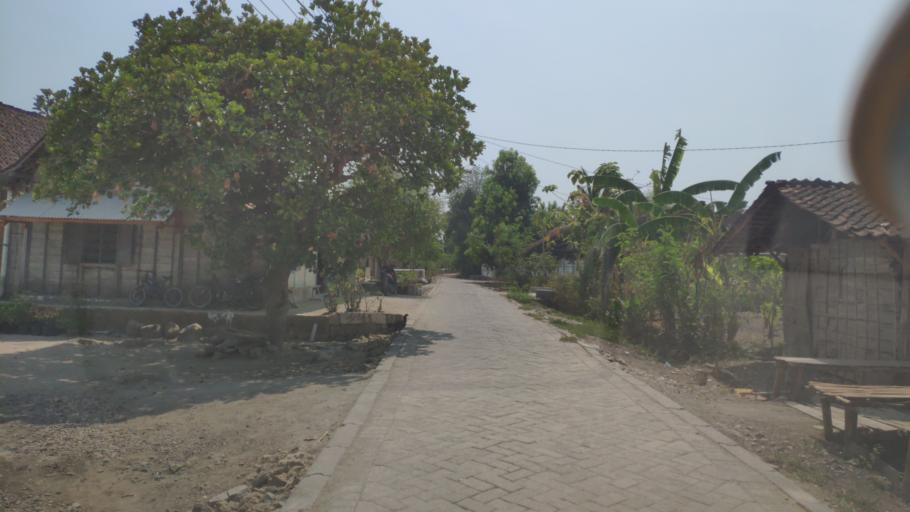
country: ID
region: Central Java
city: Mendenrejo
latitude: -7.2417
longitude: 111.4292
